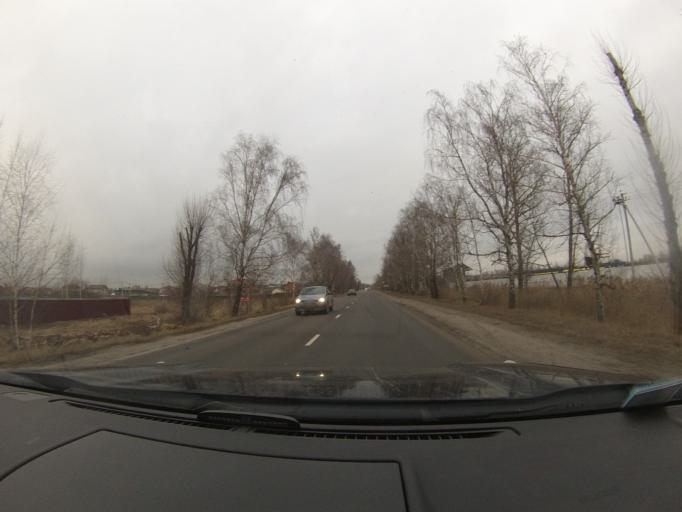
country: RU
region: Moskovskaya
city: Lopatinskiy
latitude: 55.3303
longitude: 38.7231
